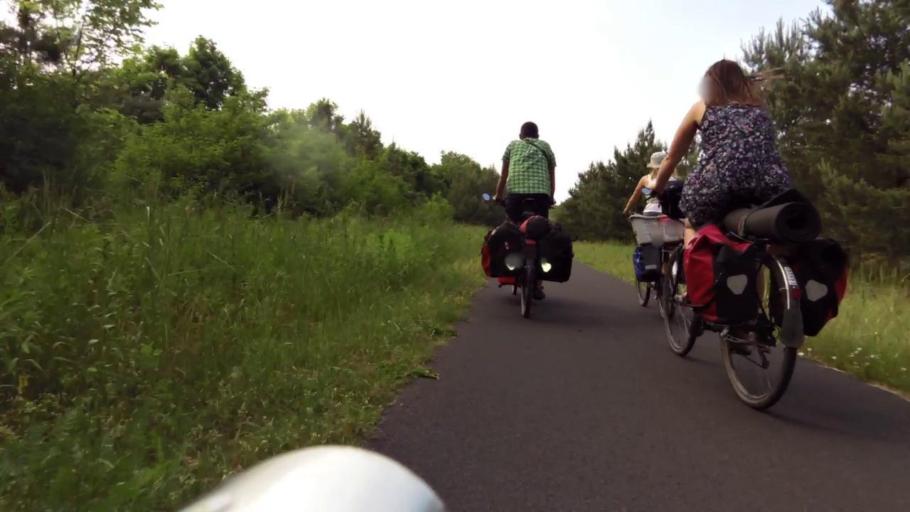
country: PL
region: Kujawsko-Pomorskie
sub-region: Powiat torunski
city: Lysomice
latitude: 53.0779
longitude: 18.5414
